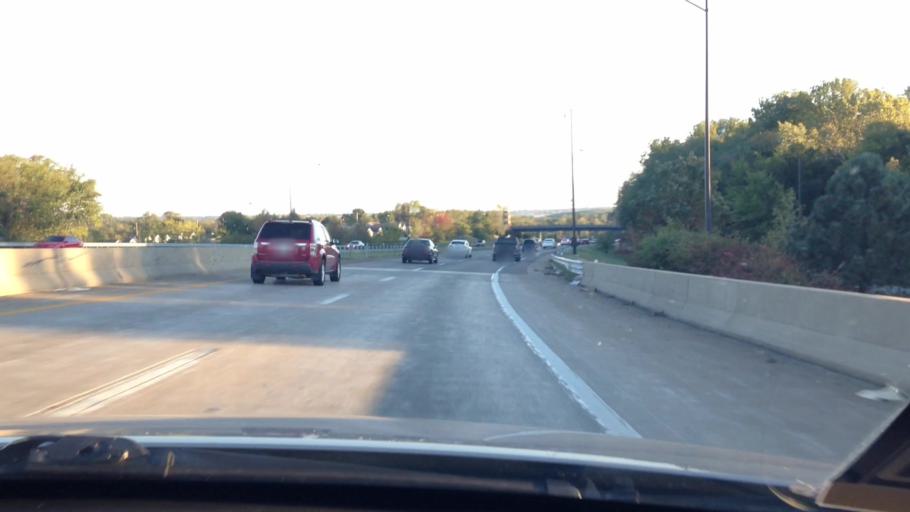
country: US
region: Kansas
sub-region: Johnson County
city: Leawood
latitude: 38.9906
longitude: -94.5529
